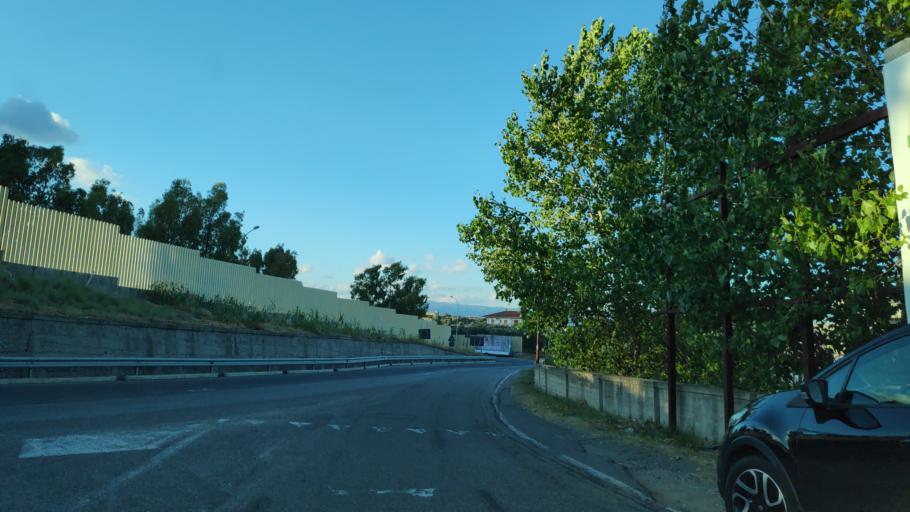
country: IT
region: Calabria
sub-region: Provincia di Reggio Calabria
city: Locri
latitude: 38.2351
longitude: 16.2475
